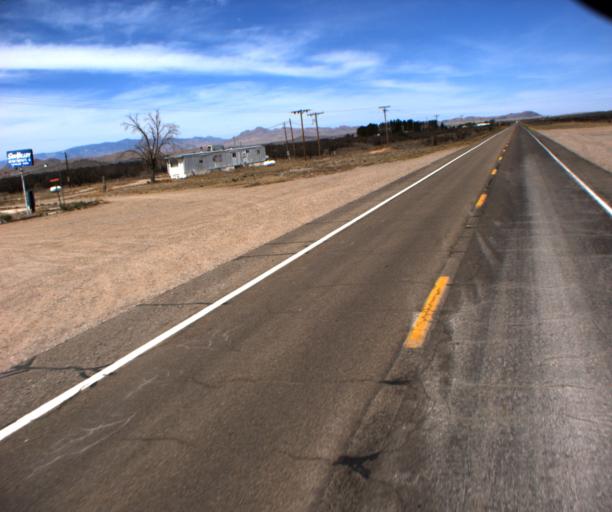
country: US
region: Arizona
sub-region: Cochise County
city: Willcox
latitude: 32.2794
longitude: -109.8139
